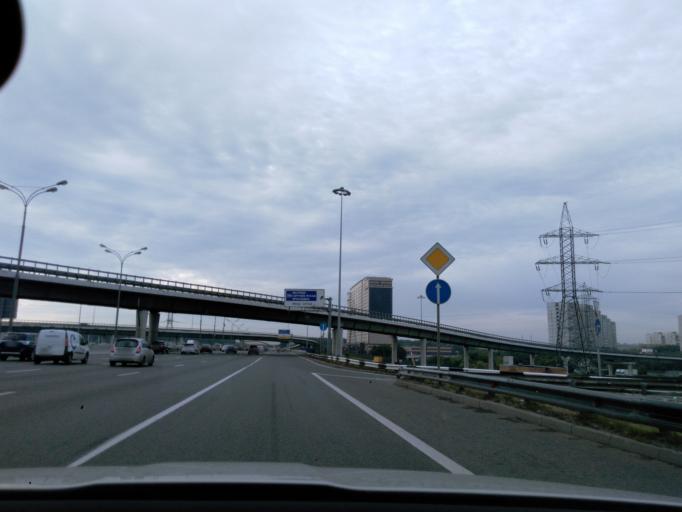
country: RU
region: Moscow
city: Yaroslavskiy
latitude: 55.8833
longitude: 37.7235
